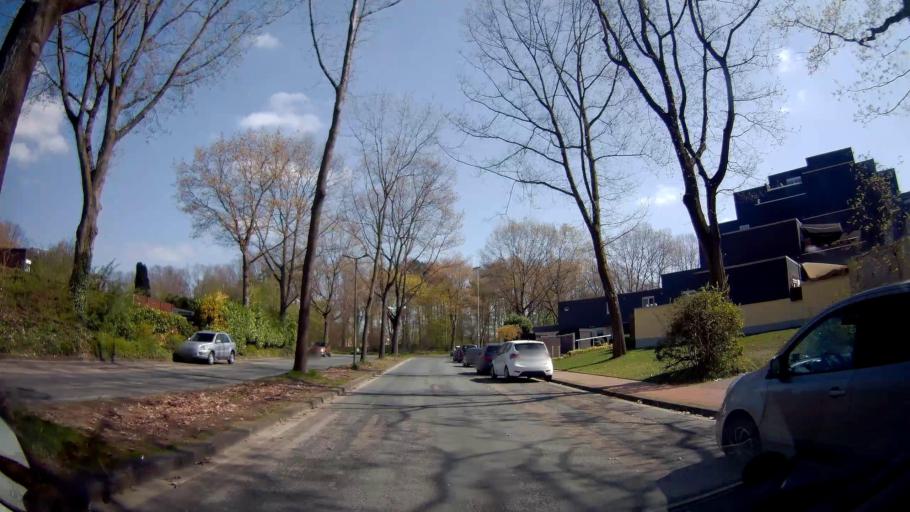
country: DE
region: North Rhine-Westphalia
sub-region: Regierungsbezirk Munster
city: Klein Reken
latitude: 51.7327
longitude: 7.0424
